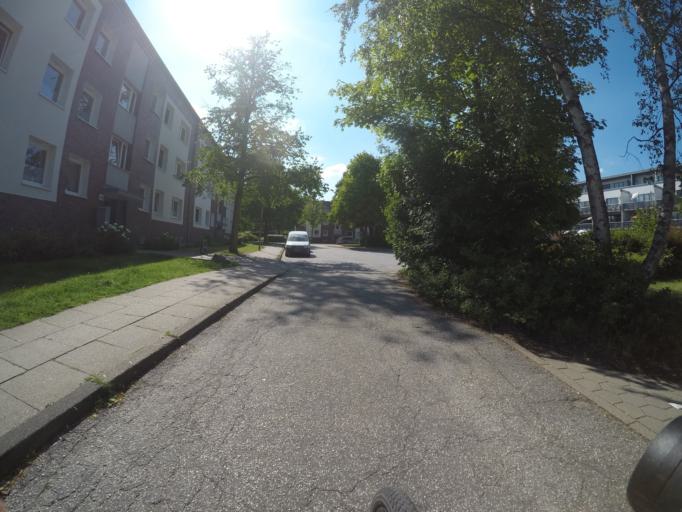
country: DE
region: Hamburg
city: Bergedorf
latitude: 53.5085
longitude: 10.2165
